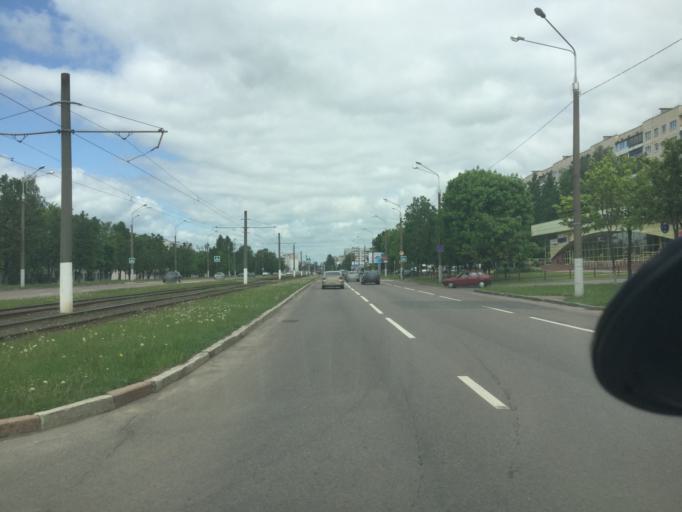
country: BY
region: Vitebsk
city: Vitebsk
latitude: 55.1798
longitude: 30.2295
